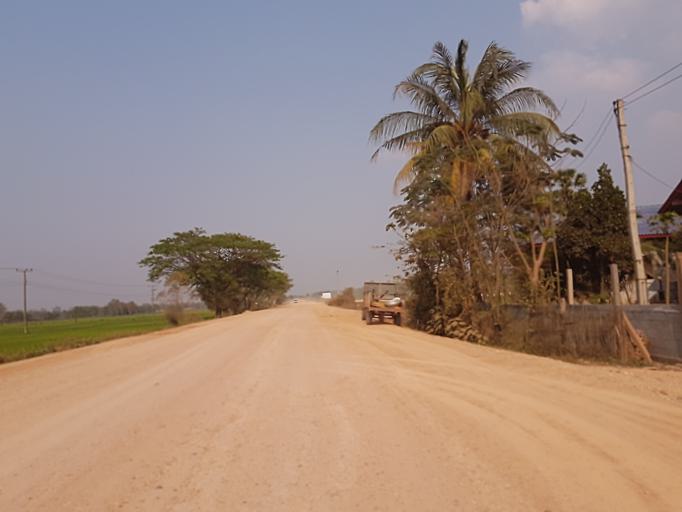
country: TH
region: Nong Khai
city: Phon Phisai
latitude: 17.9882
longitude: 102.9004
